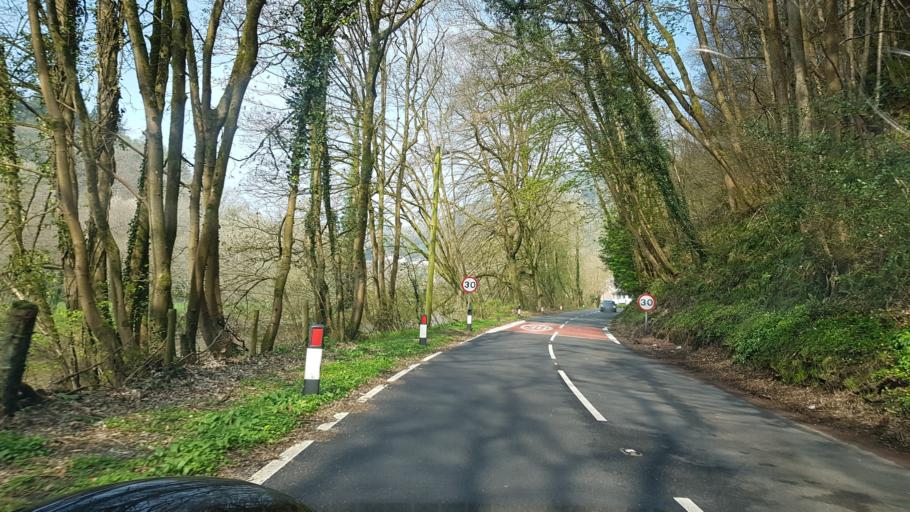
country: GB
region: Wales
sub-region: Monmouthshire
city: Monmouth
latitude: 51.7816
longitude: -2.6750
